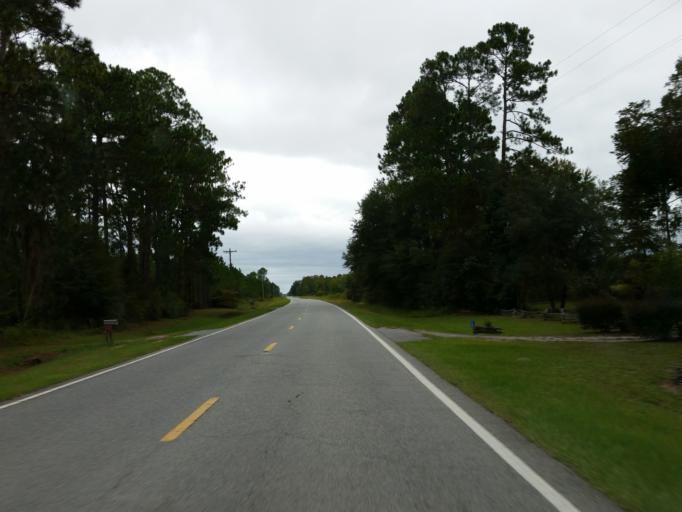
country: US
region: Georgia
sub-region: Echols County
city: Statenville
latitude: 30.8707
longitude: -83.0012
